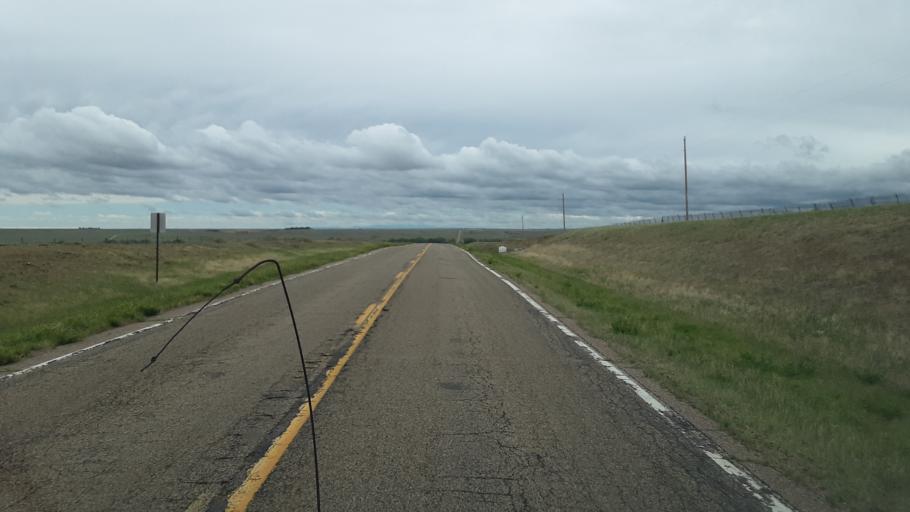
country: US
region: Colorado
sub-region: Lincoln County
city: Limon
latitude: 38.8378
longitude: -103.8236
